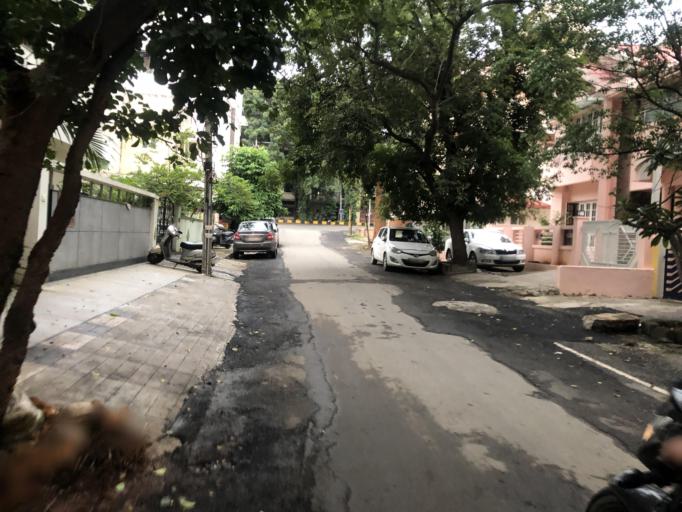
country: IN
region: Karnataka
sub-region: Bangalore Urban
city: Bangalore
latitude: 12.9415
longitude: 77.5418
